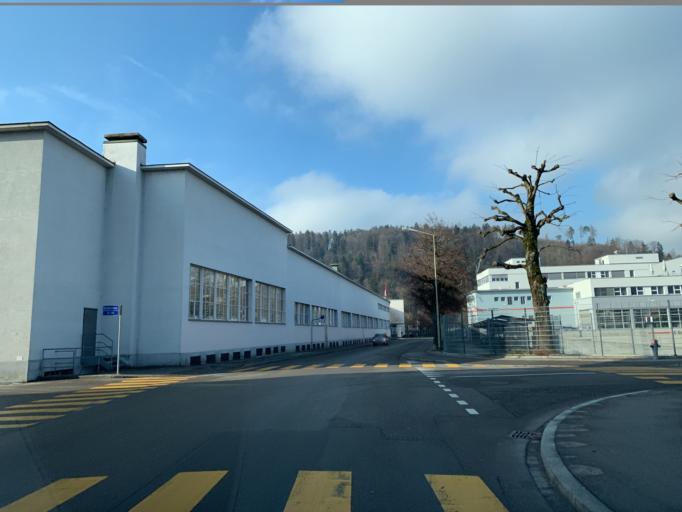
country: CH
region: Zurich
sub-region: Bezirk Winterthur
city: Toess (Kreis 4) / Eichliacker
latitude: 47.4882
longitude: 8.7071
